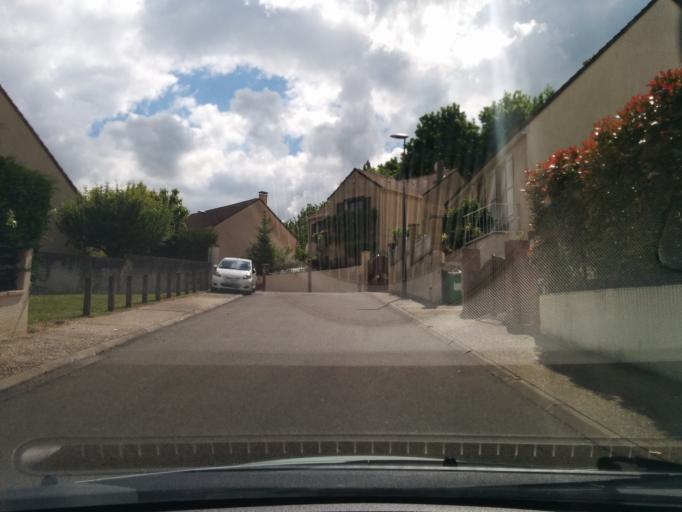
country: FR
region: Ile-de-France
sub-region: Departement des Yvelines
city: Aubergenville
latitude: 48.9570
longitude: 1.8445
